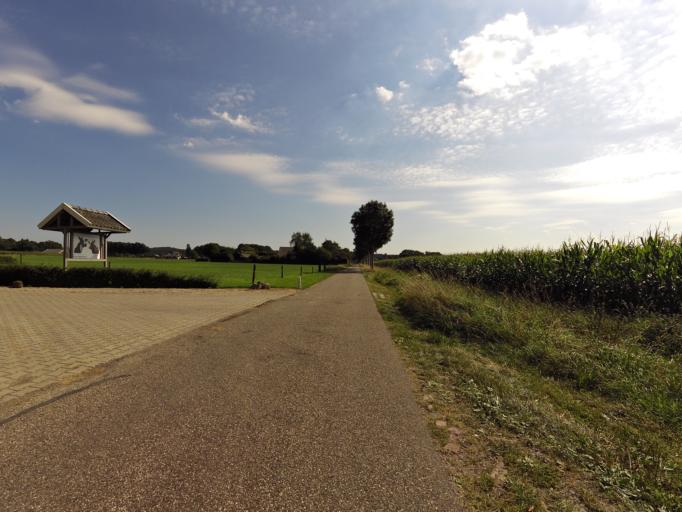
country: NL
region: Gelderland
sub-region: Gemeente Montferland
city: s-Heerenberg
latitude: 51.9273
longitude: 6.1903
